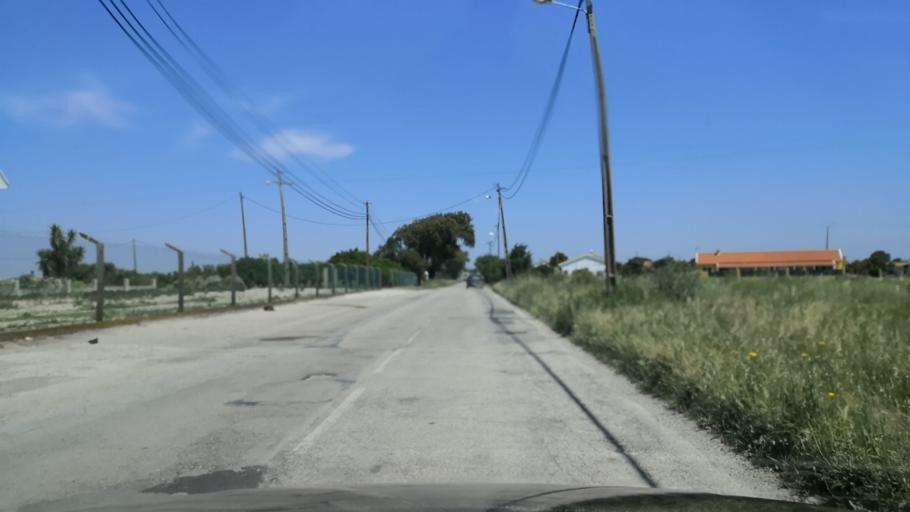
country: PT
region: Setubal
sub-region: Palmela
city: Palmela
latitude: 38.6087
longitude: -8.7742
